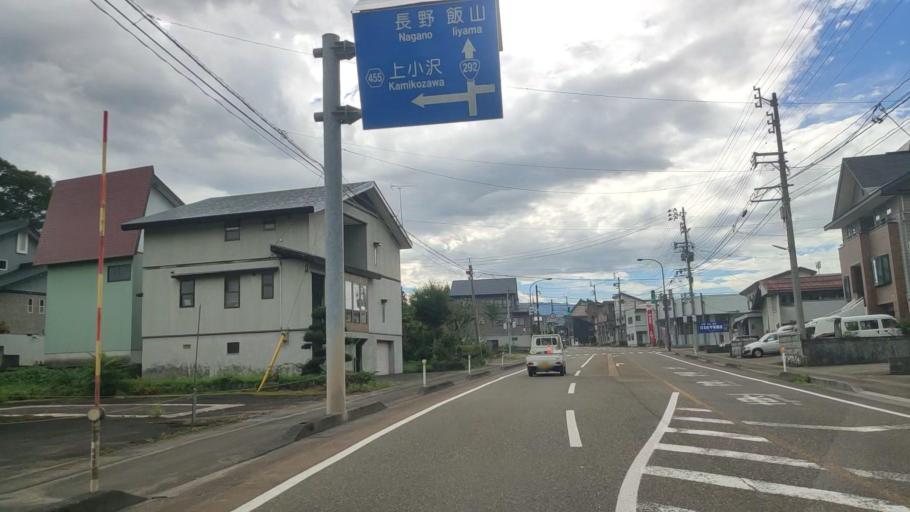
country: JP
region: Niigata
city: Arai
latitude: 36.9881
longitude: 138.2715
